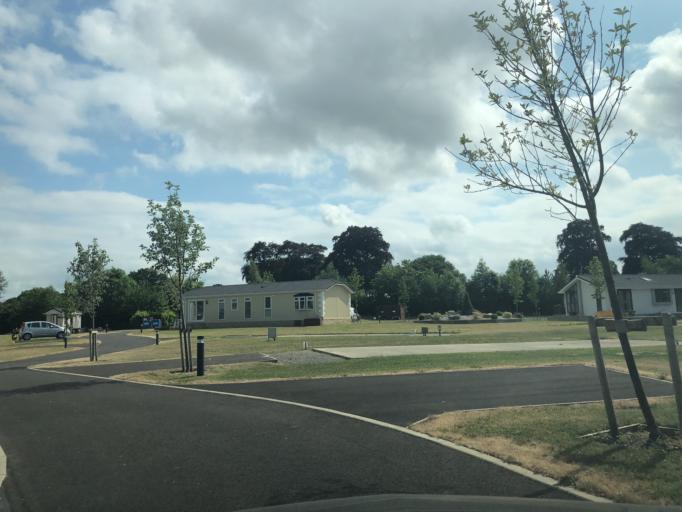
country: GB
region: England
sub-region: North Yorkshire
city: Stokesley
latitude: 54.4588
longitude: -1.2662
